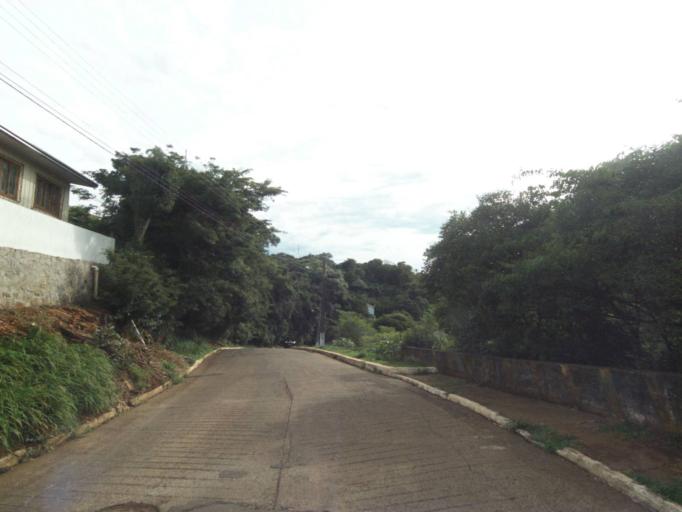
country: BR
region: Parana
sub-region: Guaraniacu
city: Guaraniacu
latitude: -25.1015
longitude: -52.8715
